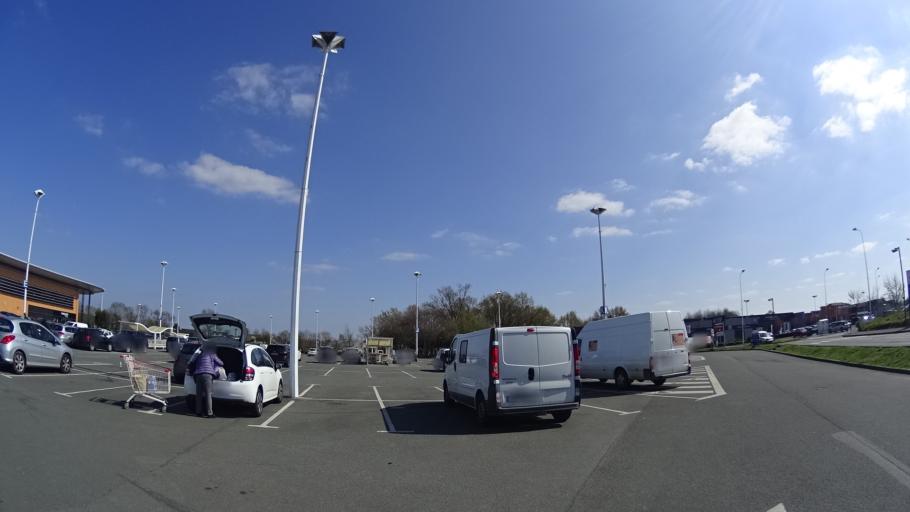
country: FR
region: Pays de la Loire
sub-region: Departement de Maine-et-Loire
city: Murs-Erigne
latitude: 47.3977
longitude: -0.5292
